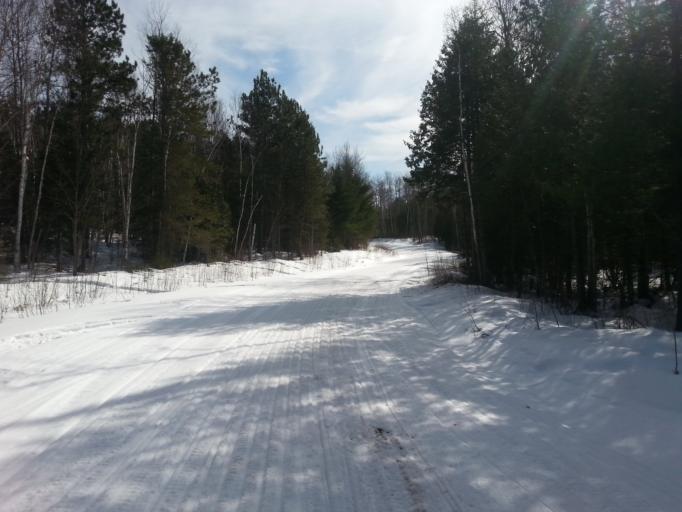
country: CA
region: Ontario
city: Greater Sudbury
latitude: 46.3426
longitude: -80.9023
